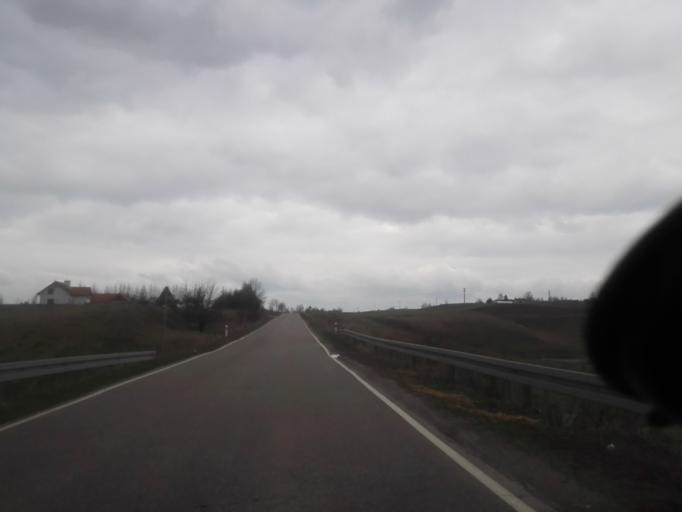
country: PL
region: Podlasie
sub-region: Suwalki
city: Suwalki
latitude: 54.2257
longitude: 22.9119
